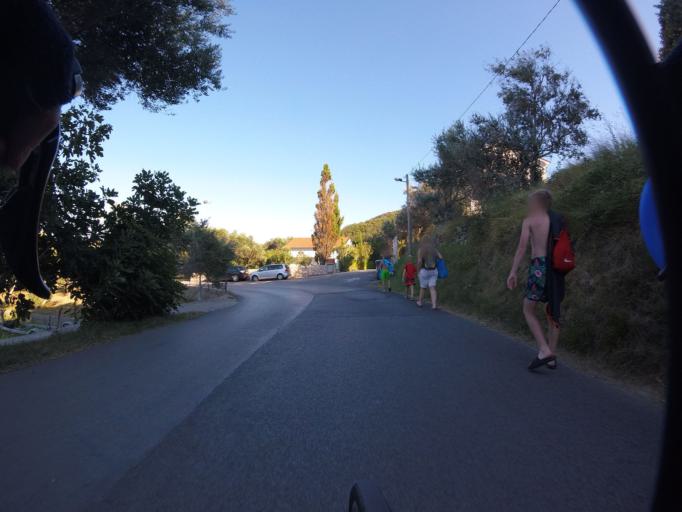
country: HR
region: Primorsko-Goranska
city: Supetarska Draga
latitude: 44.7992
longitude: 14.7154
